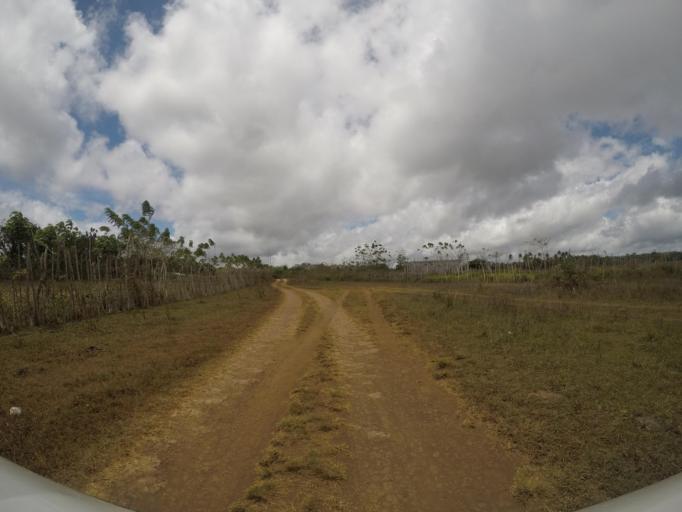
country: TL
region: Lautem
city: Lospalos
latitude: -8.4733
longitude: 126.9890
